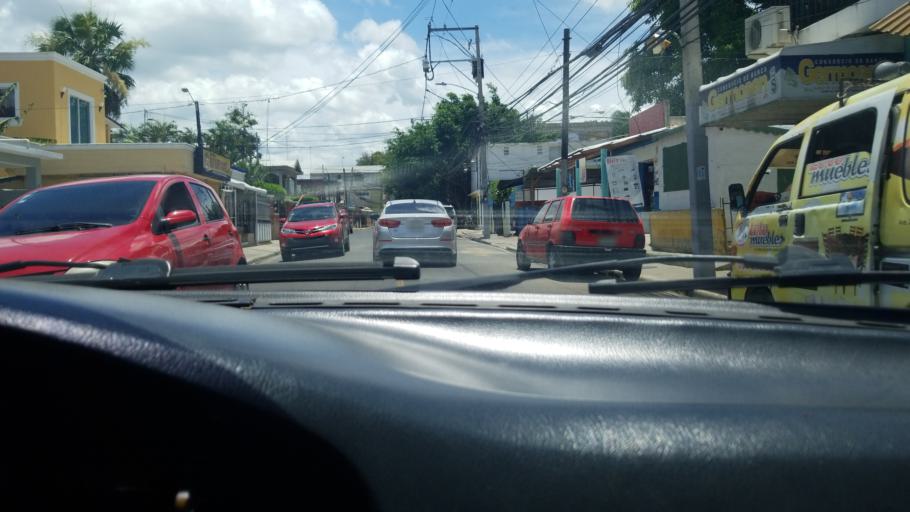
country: DO
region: Santiago
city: Santiago de los Caballeros
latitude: 19.4720
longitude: -70.6875
